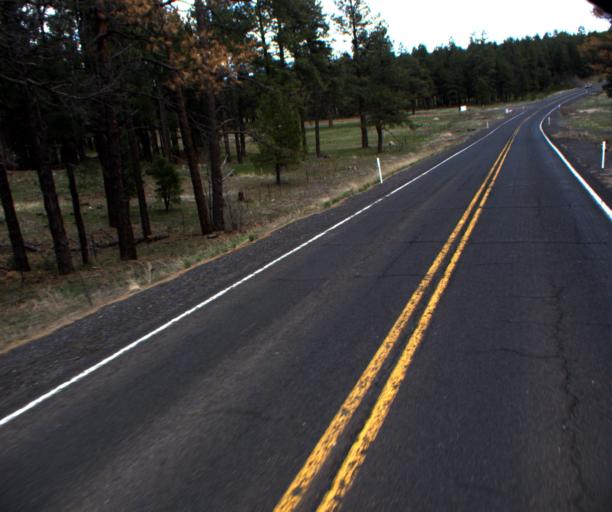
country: US
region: Arizona
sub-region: Coconino County
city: Kachina Village
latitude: 35.1181
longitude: -111.7098
